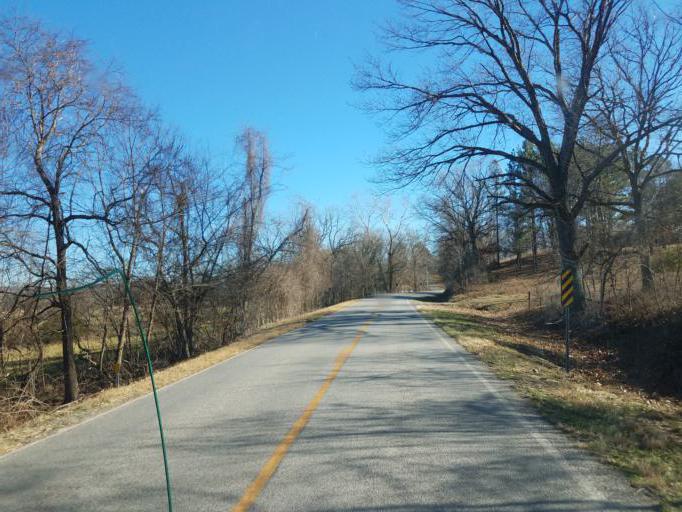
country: US
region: Arkansas
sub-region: Washington County
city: Elkins
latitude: 36.0325
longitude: -93.9437
